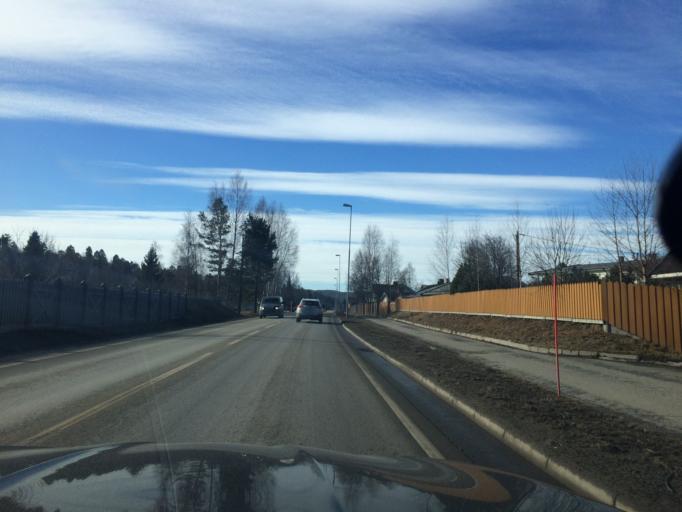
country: NO
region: Hedmark
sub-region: Elverum
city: Elverum
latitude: 60.8895
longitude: 11.5723
